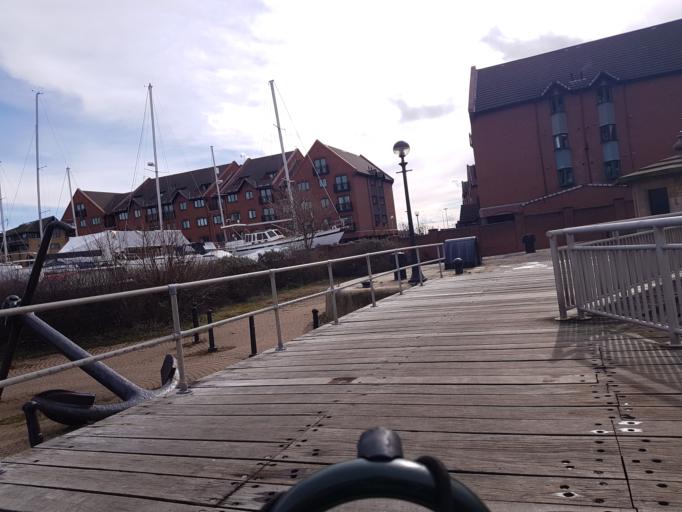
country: GB
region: England
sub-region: Liverpool
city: Liverpool
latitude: 53.3887
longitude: -2.9862
